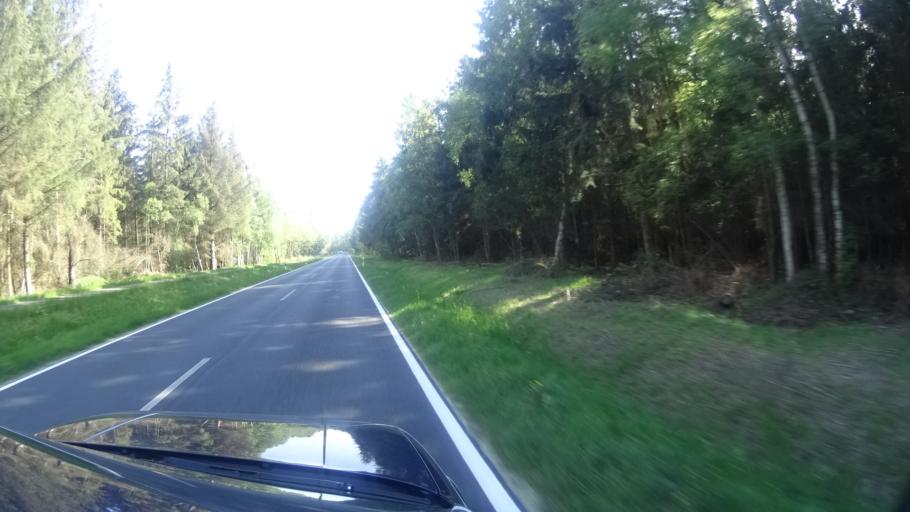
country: DE
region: Mecklenburg-Vorpommern
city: Ostseebad Prerow
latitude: 54.4275
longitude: 12.5731
